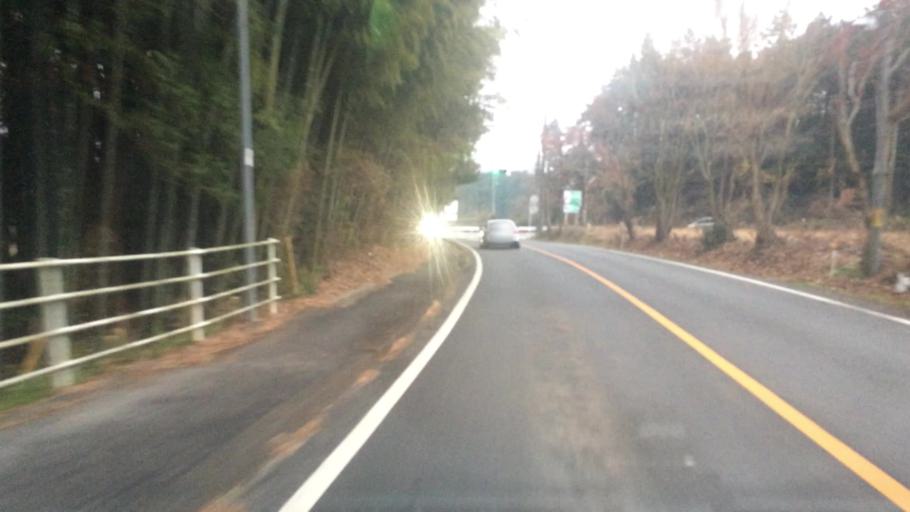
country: JP
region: Tochigi
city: Imaichi
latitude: 36.6705
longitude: 139.7737
